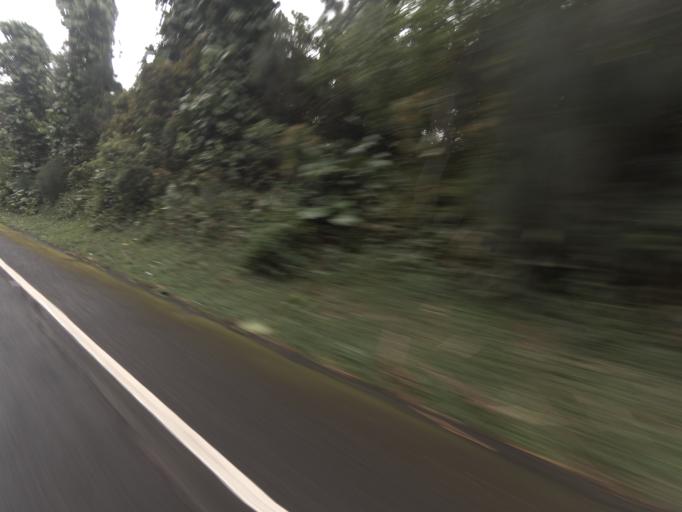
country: US
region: Hawaii
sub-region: Honolulu County
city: Kane'ohe
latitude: 21.3738
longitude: -157.8236
